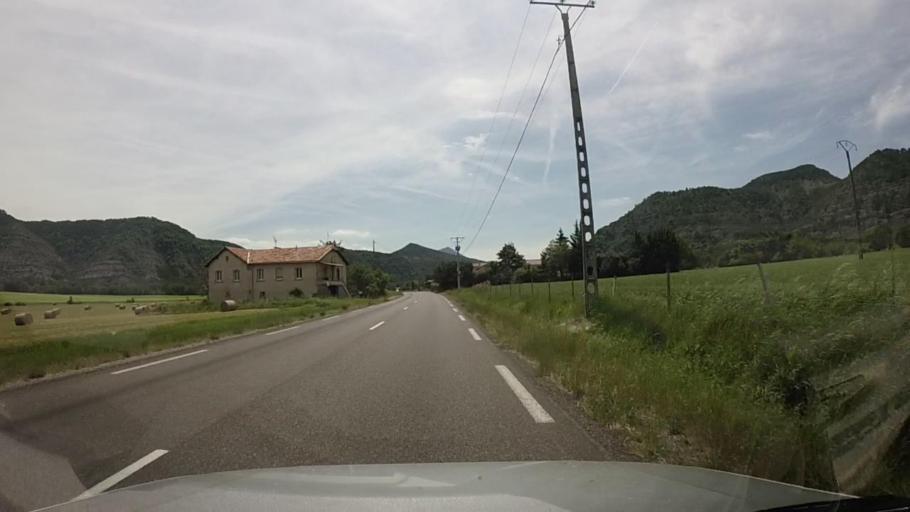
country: FR
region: Provence-Alpes-Cote d'Azur
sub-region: Departement des Alpes-de-Haute-Provence
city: Le Brusquet
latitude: 44.1259
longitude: 6.2809
